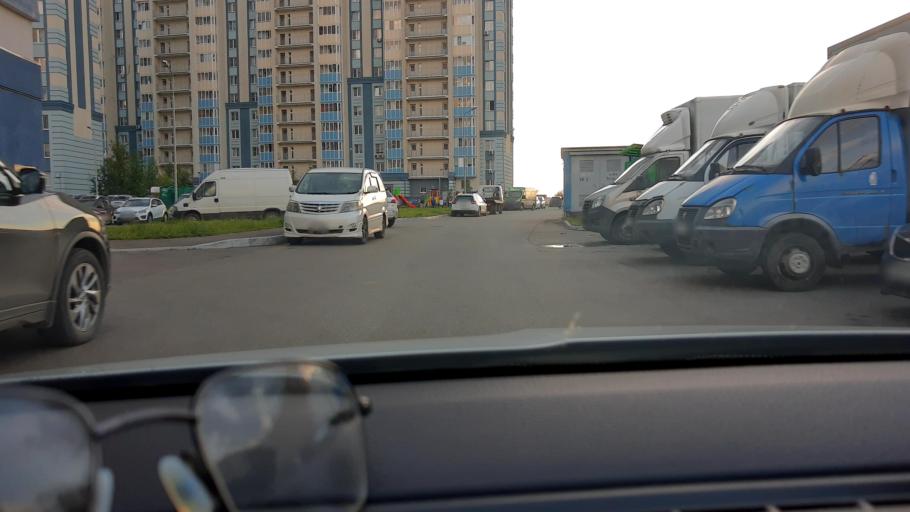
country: RU
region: Moskovskaya
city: Domodedovo
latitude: 55.4045
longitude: 37.7677
